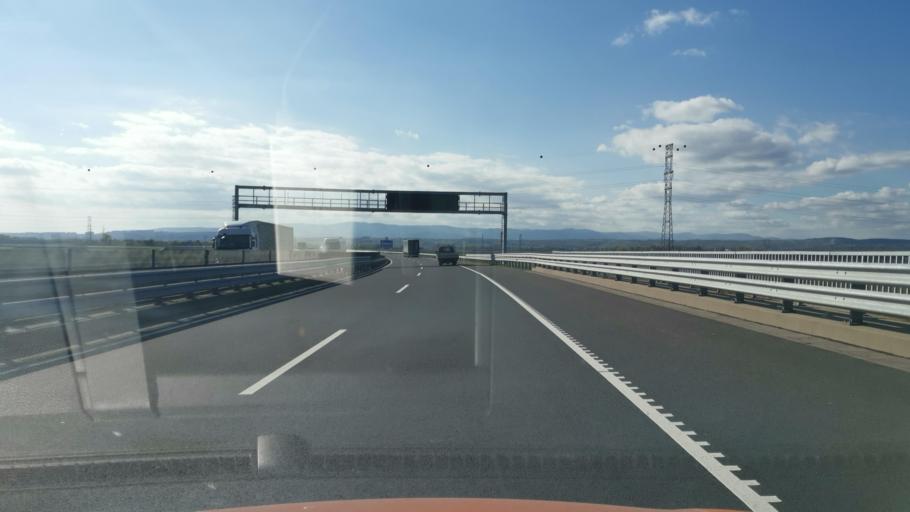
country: HU
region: Borsod-Abauj-Zemplen
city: Arnot
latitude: 48.1443
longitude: 20.8421
